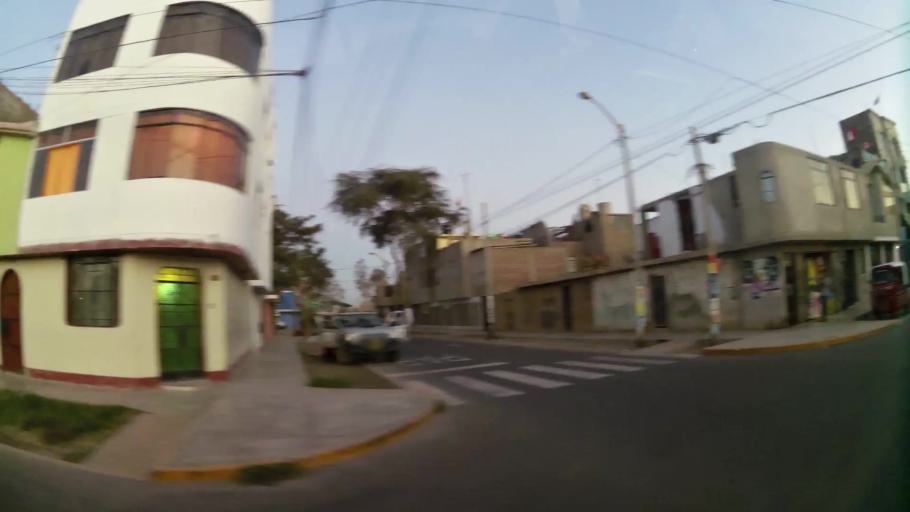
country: PE
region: Ica
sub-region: Provincia de Ica
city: Ica
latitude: -14.0821
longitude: -75.7327
